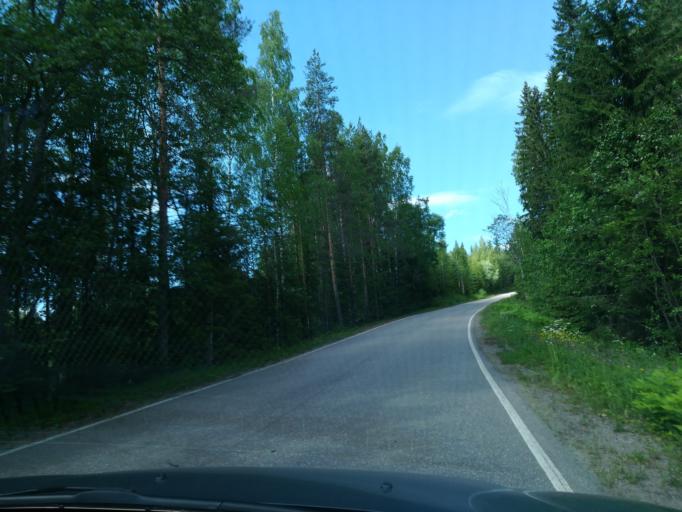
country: FI
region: South Karelia
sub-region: Imatra
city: Ruokolahti
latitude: 61.4837
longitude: 28.8733
